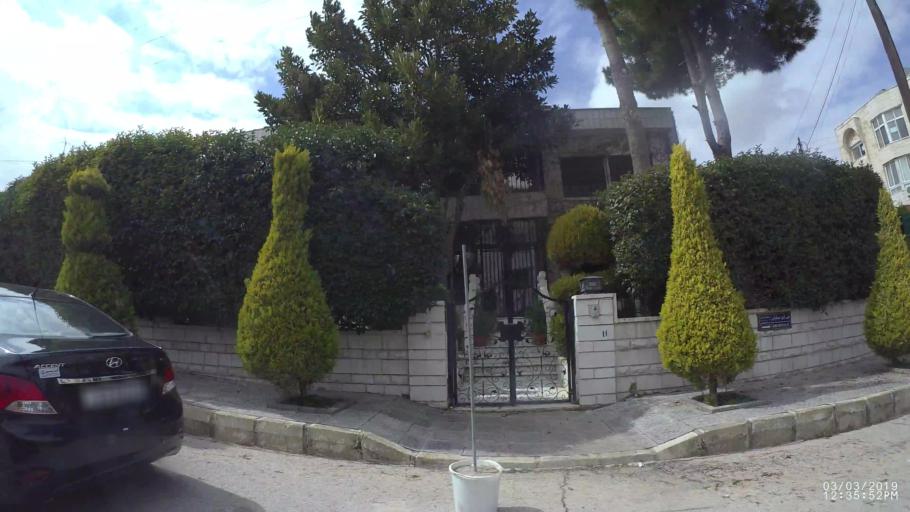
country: JO
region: Amman
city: Amman
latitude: 31.9751
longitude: 35.9026
